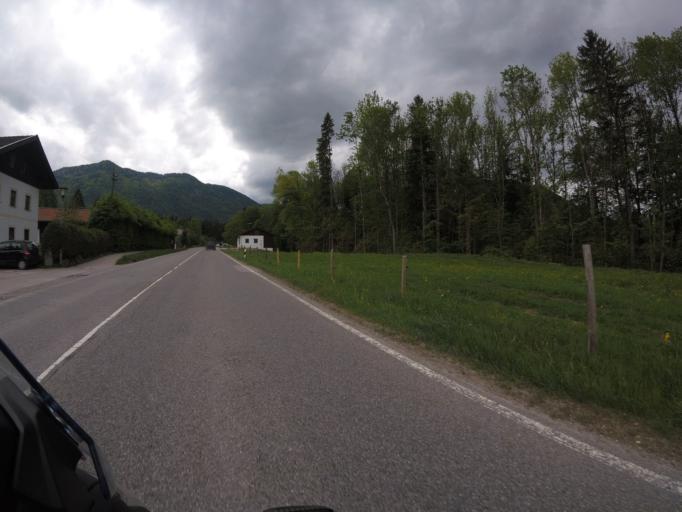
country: DE
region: Bavaria
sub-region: Upper Bavaria
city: Lenggries
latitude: 47.6353
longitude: 11.5943
